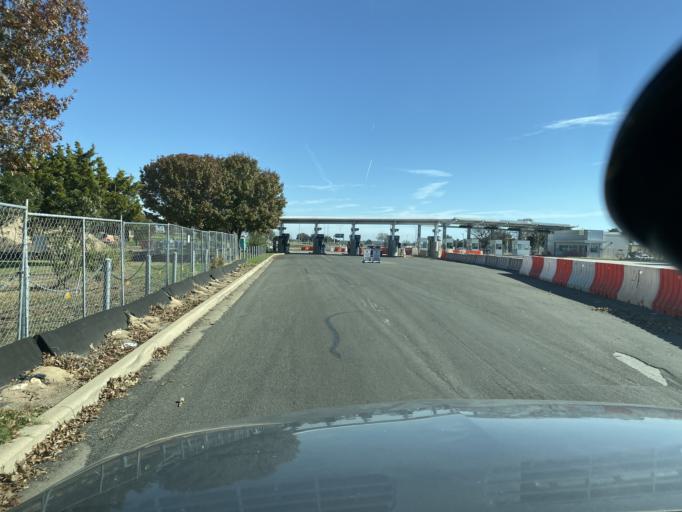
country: US
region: Texas
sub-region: Travis County
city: Hornsby Bend
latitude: 30.2094
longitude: -97.6668
